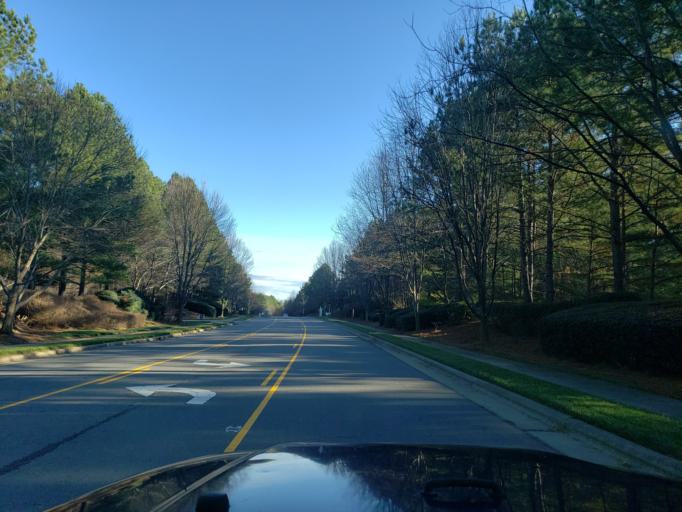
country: US
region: North Carolina
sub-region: Catawba County
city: Lake Norman of Catawba
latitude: 35.5474
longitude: -80.9215
